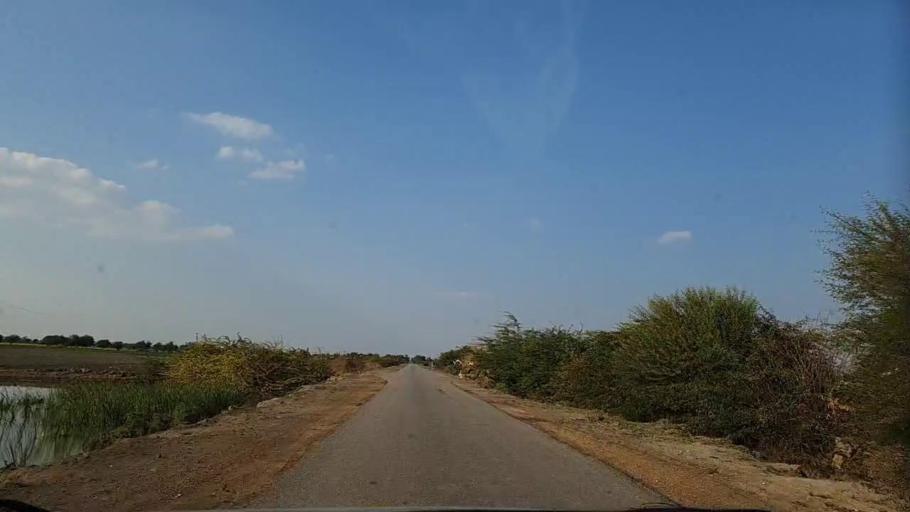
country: PK
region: Sindh
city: Pithoro
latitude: 25.7194
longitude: 69.2175
